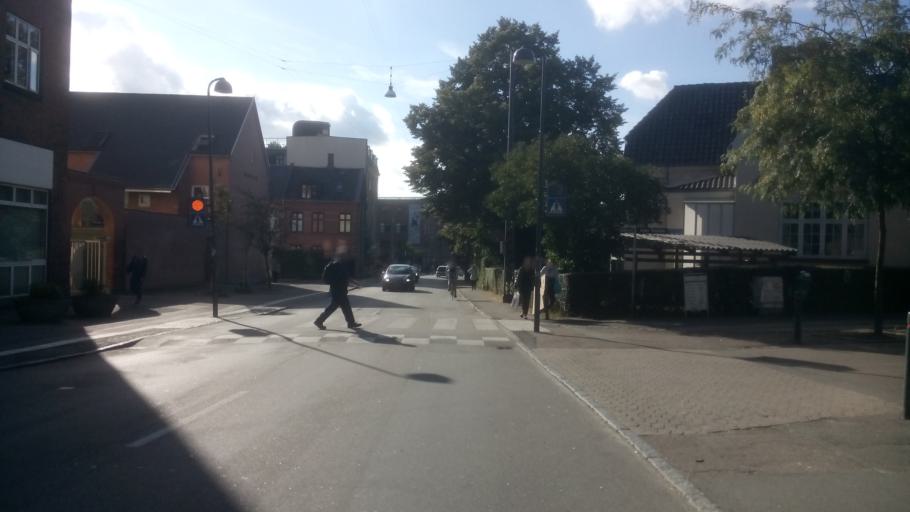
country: DK
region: Capital Region
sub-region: Frederiksberg Kommune
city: Frederiksberg
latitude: 55.6650
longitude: 12.5149
